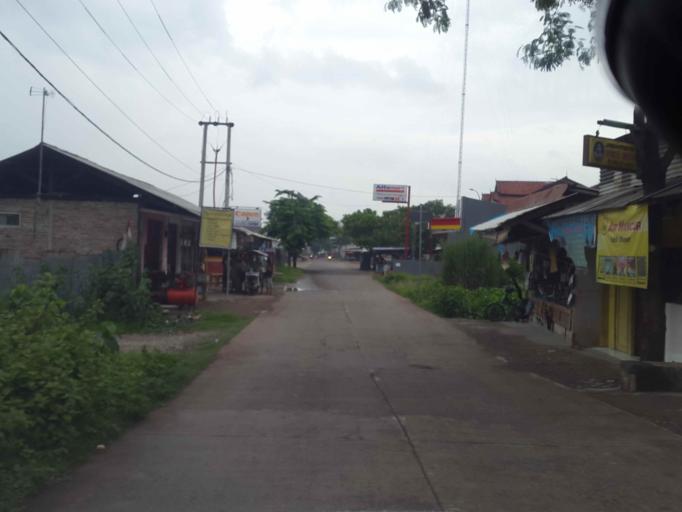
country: ID
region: West Java
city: Cikarang
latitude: -6.2906
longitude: 107.1795
